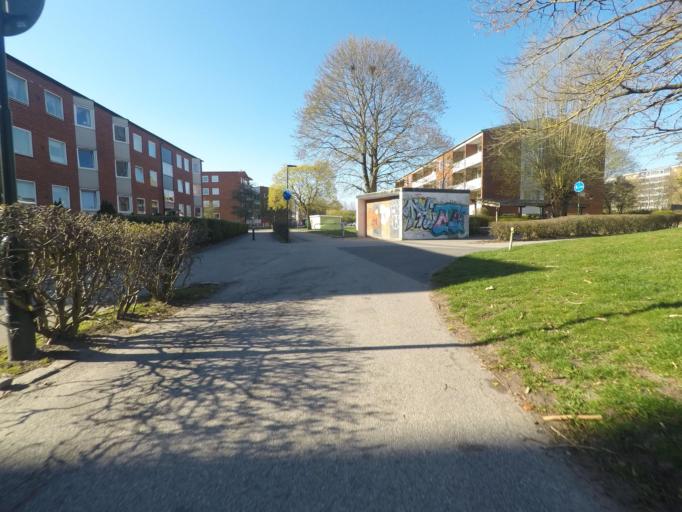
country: SE
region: Skane
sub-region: Malmo
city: Malmoe
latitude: 55.5664
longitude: 13.0162
